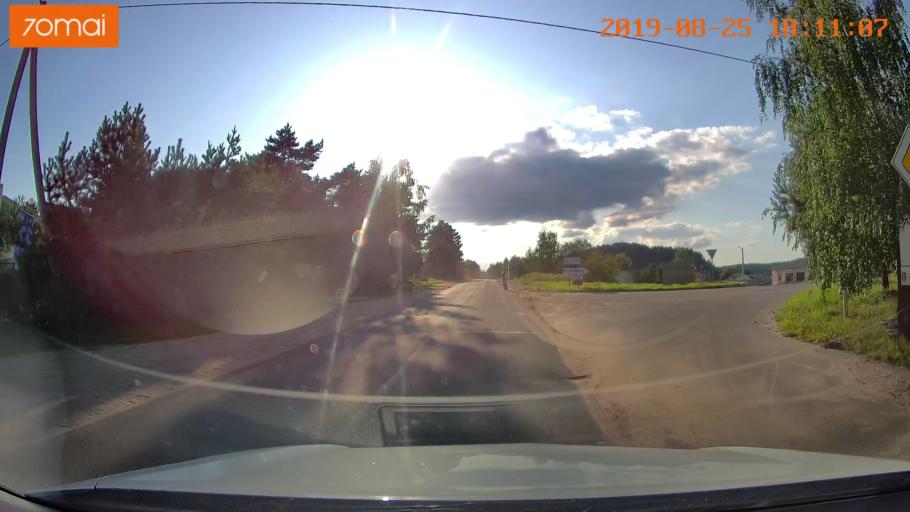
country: BY
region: Minsk
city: Khatsyezhyna
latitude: 53.9399
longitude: 27.3208
